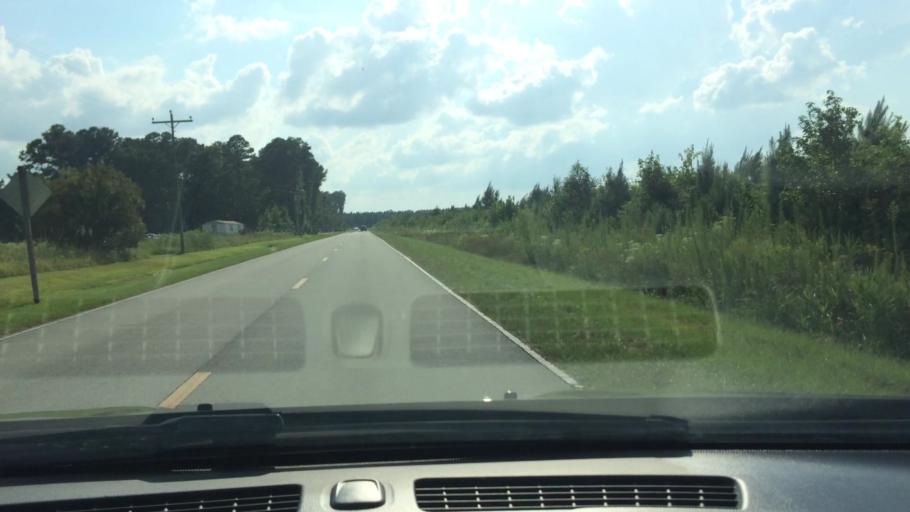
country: US
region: North Carolina
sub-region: Beaufort County
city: River Road
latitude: 35.4366
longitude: -77.0007
